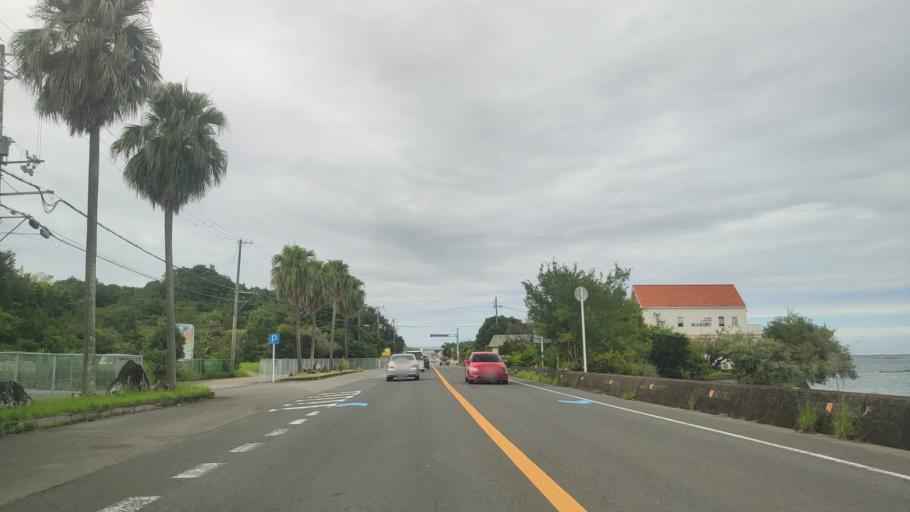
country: JP
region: Wakayama
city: Tanabe
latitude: 33.7021
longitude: 135.3939
